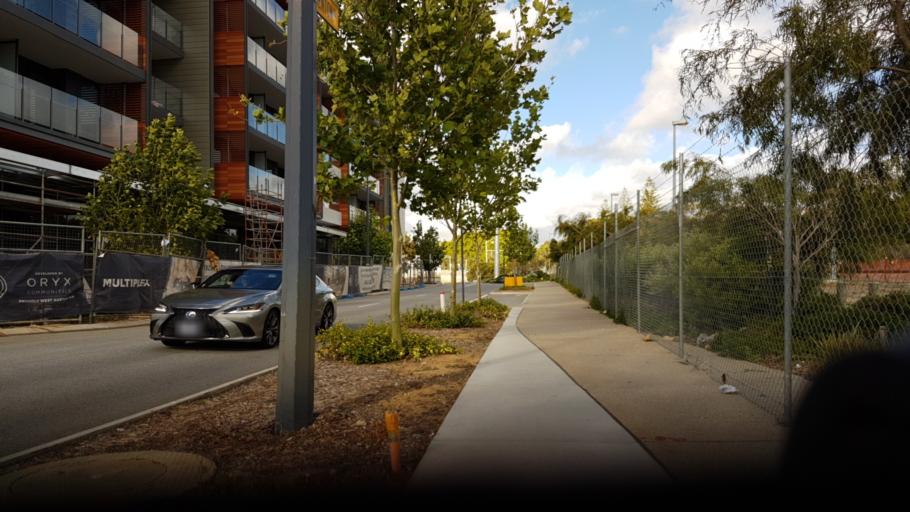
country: AU
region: Western Australia
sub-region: Claremont
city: Claremont
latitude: -31.9792
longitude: 115.7840
